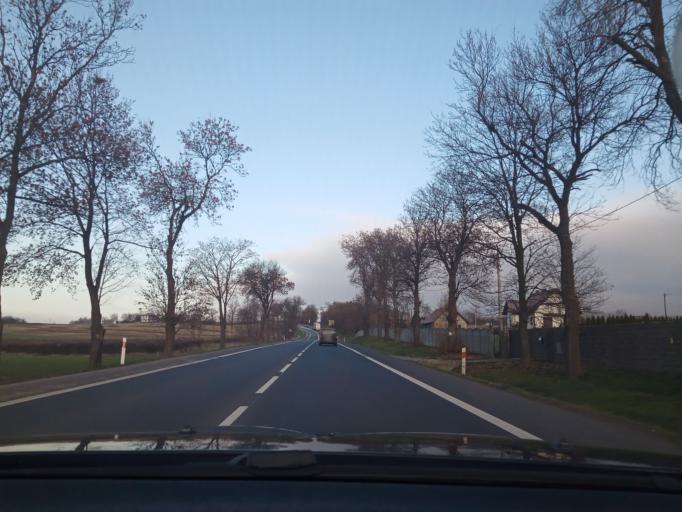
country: PL
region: Lesser Poland Voivodeship
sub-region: Powiat krakowski
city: Slomniki
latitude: 50.2882
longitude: 20.0501
